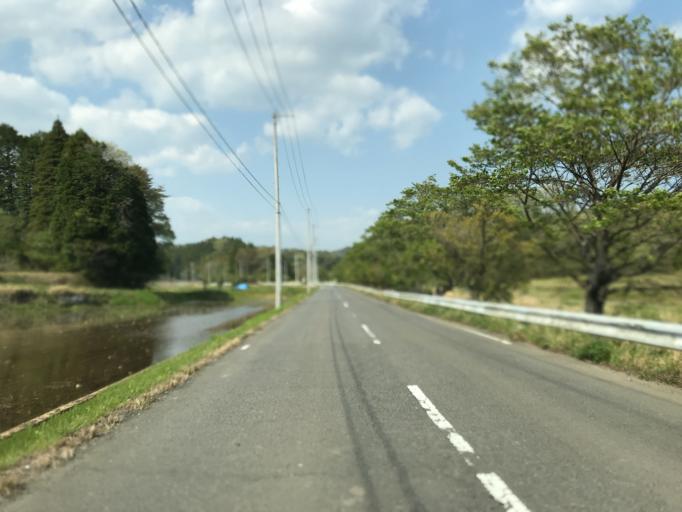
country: JP
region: Fukushima
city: Iwaki
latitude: 36.9638
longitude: 140.7554
